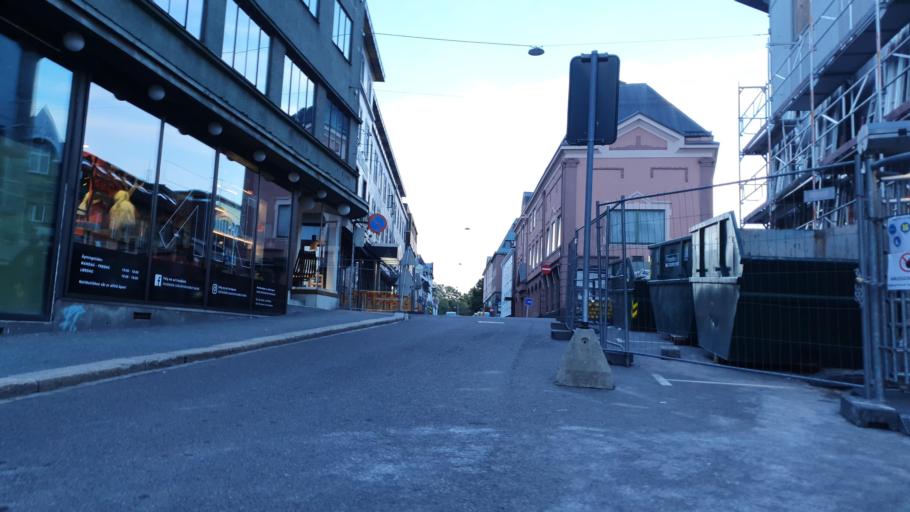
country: NO
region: Vestfold
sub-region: Tonsberg
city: Tonsberg
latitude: 59.2683
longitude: 10.4067
